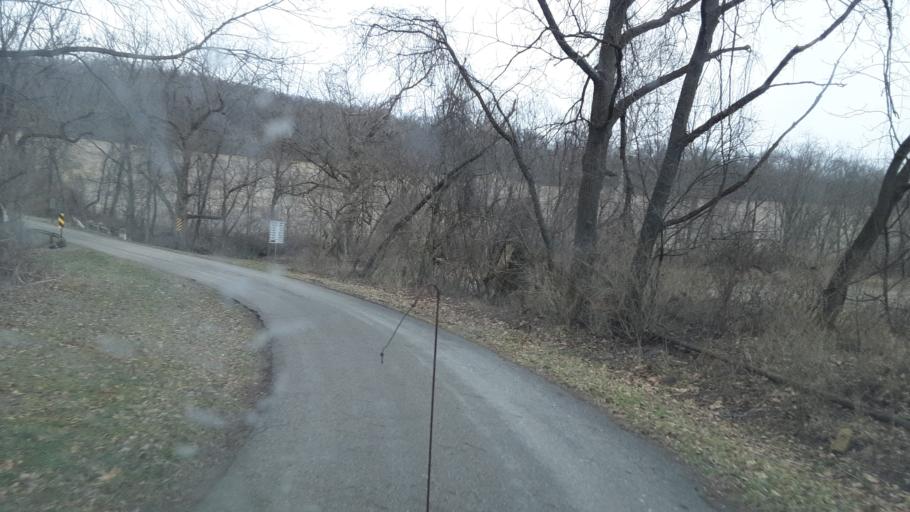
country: US
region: Ohio
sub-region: Perry County
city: Thornport
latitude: 39.9368
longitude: -82.3612
